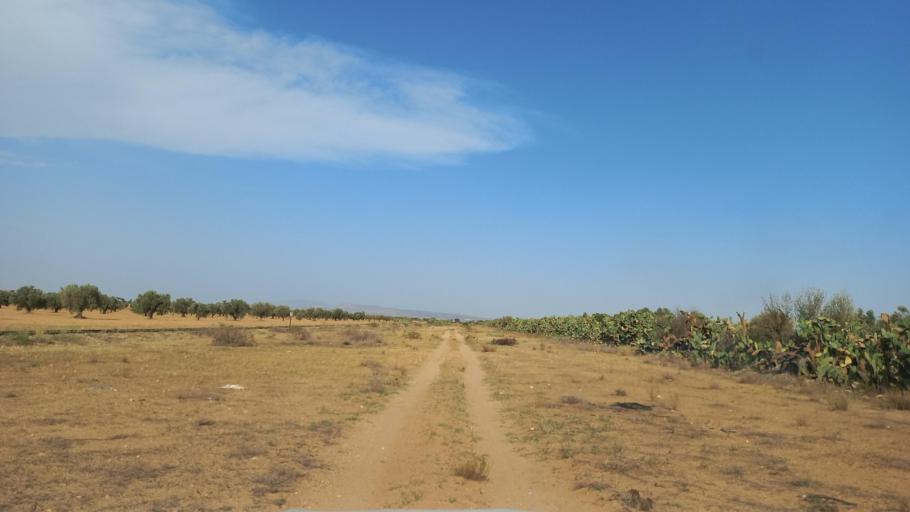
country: TN
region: Al Qasrayn
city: Kasserine
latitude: 35.2175
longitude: 8.9502
